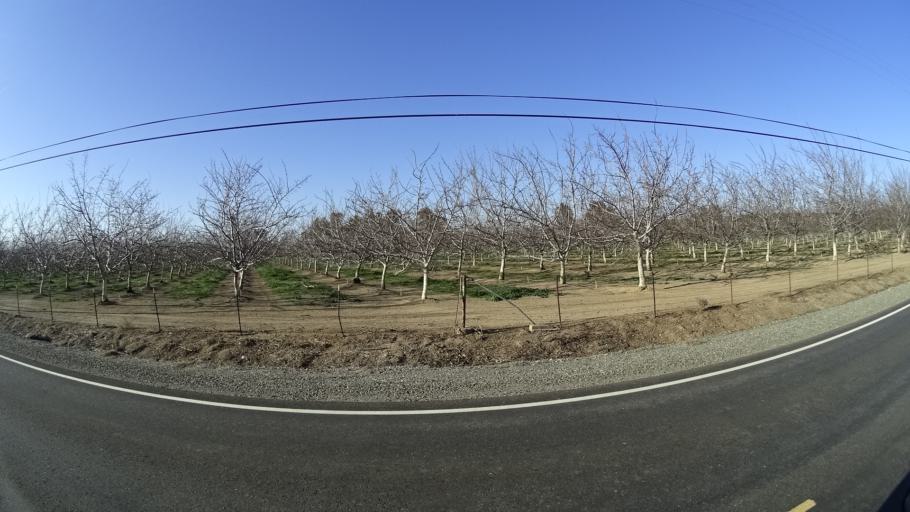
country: US
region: California
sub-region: Glenn County
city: Orland
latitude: 39.7771
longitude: -122.2782
